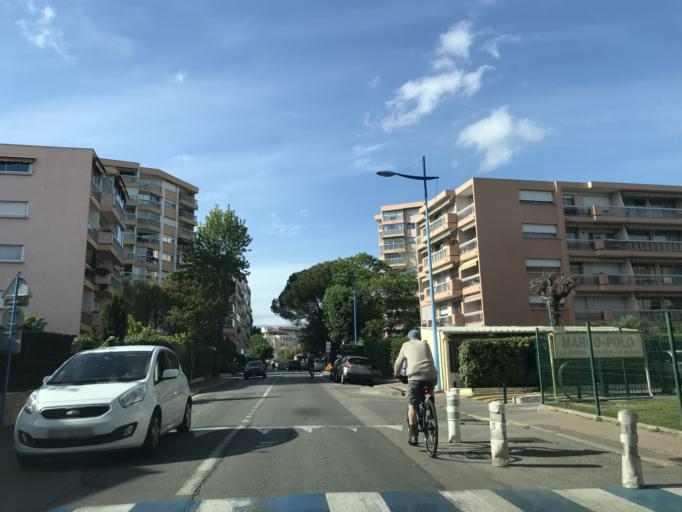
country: FR
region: Provence-Alpes-Cote d'Azur
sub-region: Departement des Alpes-Maritimes
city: Mandelieu-la-Napoule
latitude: 43.5428
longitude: 6.9424
